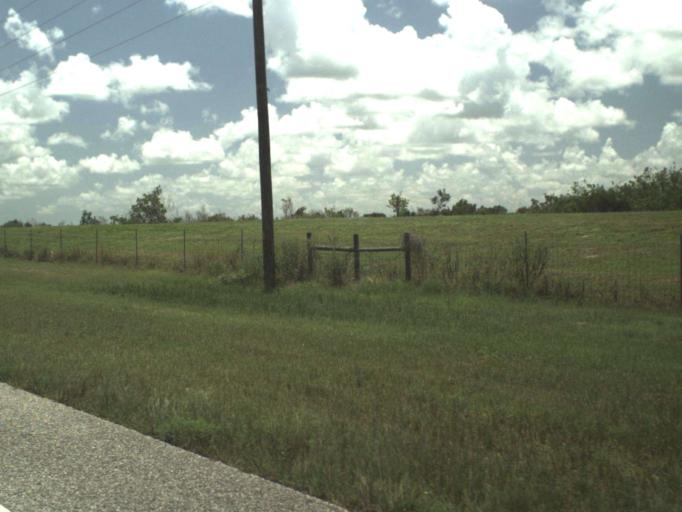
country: US
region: Florida
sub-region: Indian River County
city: Fellsmere
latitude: 27.6410
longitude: -80.7113
